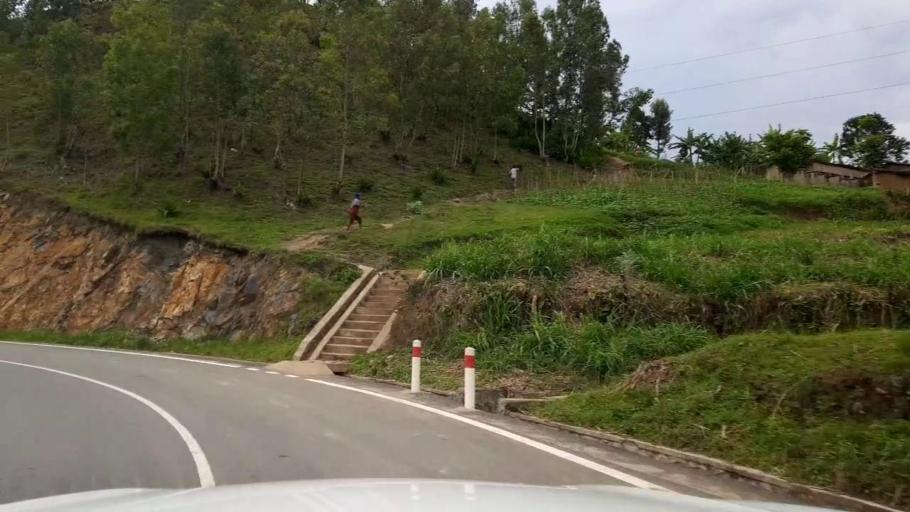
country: RW
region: Western Province
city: Kibuye
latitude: -2.0302
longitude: 29.3986
